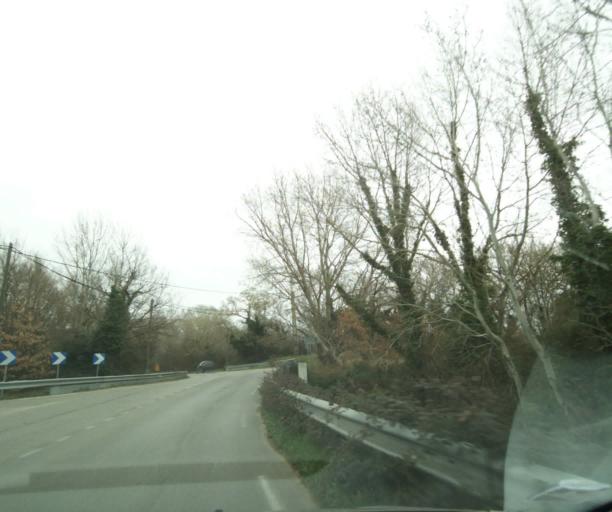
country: FR
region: Provence-Alpes-Cote d'Azur
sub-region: Departement des Bouches-du-Rhone
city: Venelles
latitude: 43.5784
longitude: 5.4390
